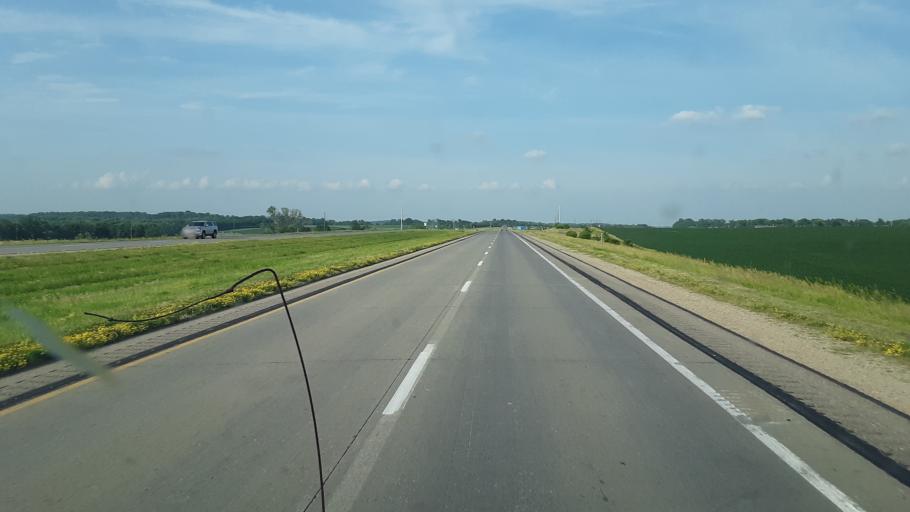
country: US
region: Iowa
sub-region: Marshall County
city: Marshalltown
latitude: 42.0079
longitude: -92.8014
